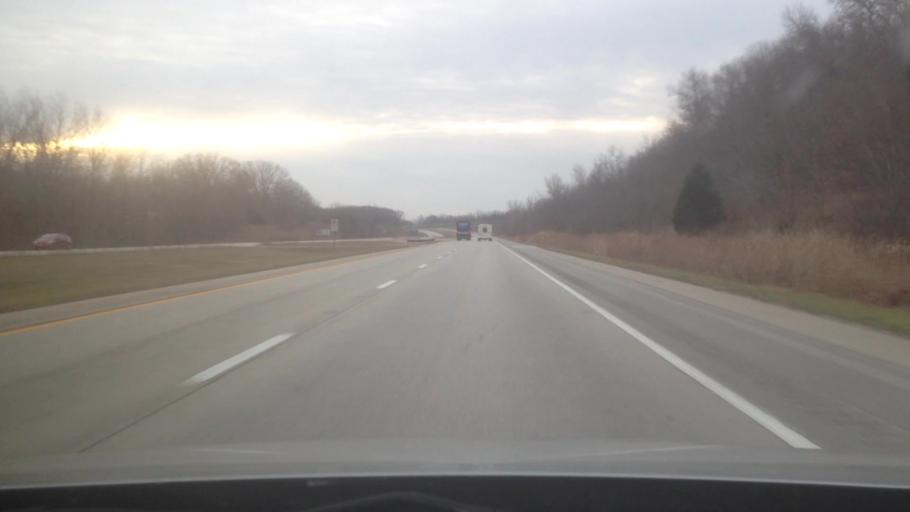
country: US
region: Illinois
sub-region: Macon County
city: Harristown
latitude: 39.8194
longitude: -89.0336
